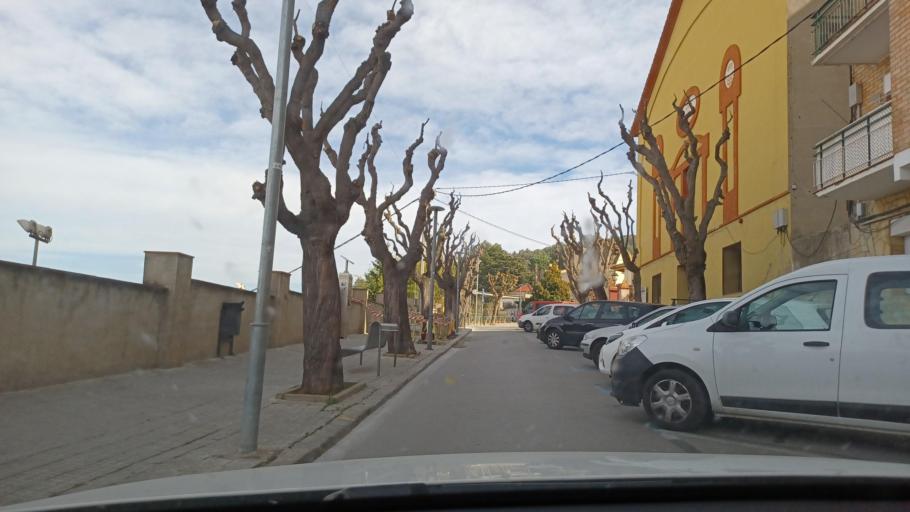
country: ES
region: Catalonia
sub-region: Provincia de Barcelona
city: Gelida
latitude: 41.4406
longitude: 1.8640
